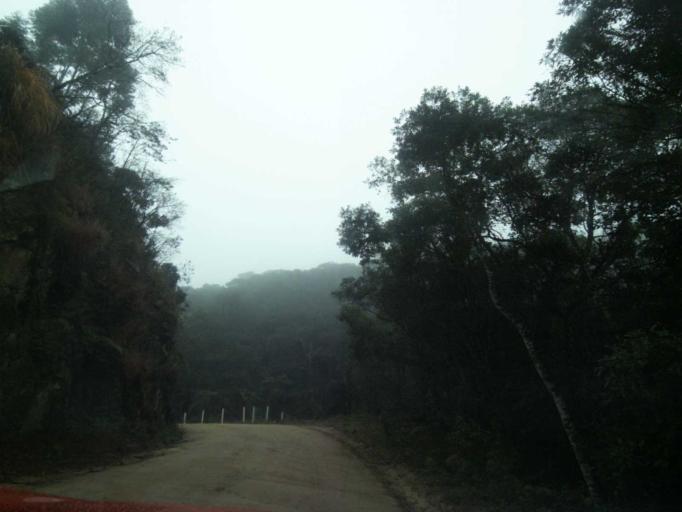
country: BR
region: Santa Catarina
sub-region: Anitapolis
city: Anitapolis
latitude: -27.9012
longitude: -49.1597
